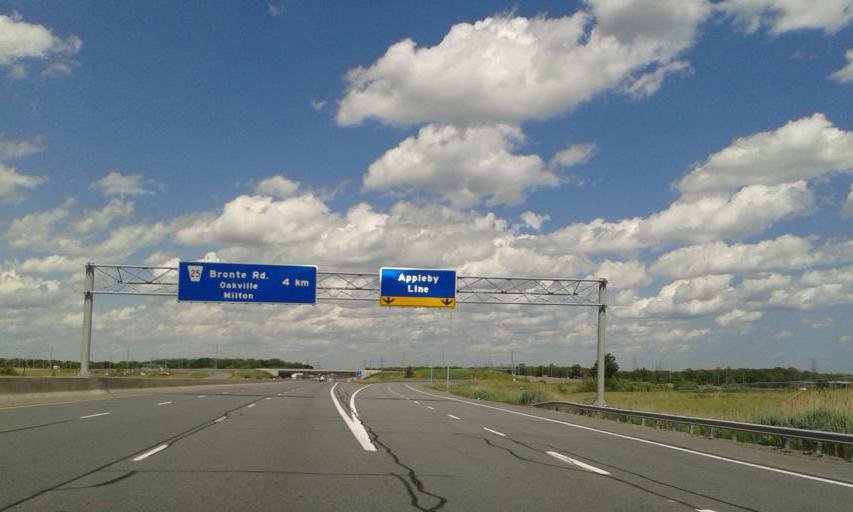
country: CA
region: Ontario
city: Burlington
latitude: 43.4106
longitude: -79.8254
